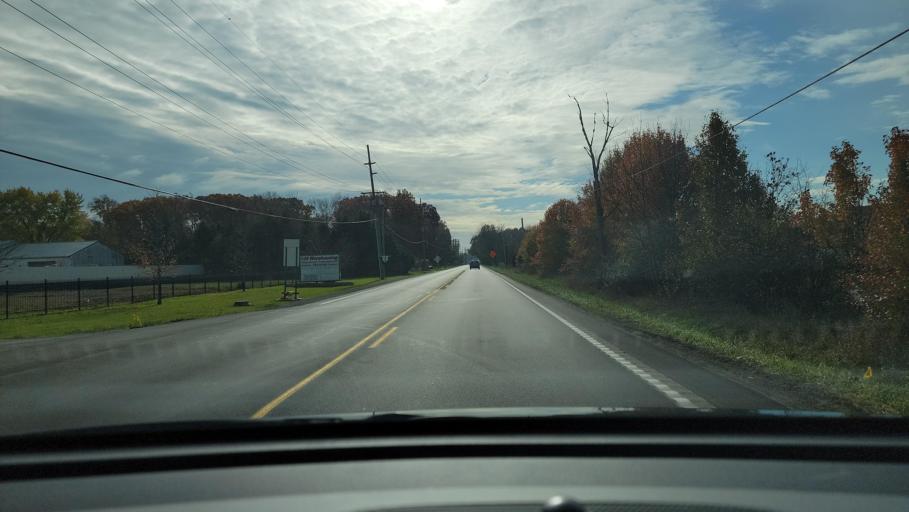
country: US
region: Indiana
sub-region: Porter County
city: South Haven
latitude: 41.5832
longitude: -87.1245
